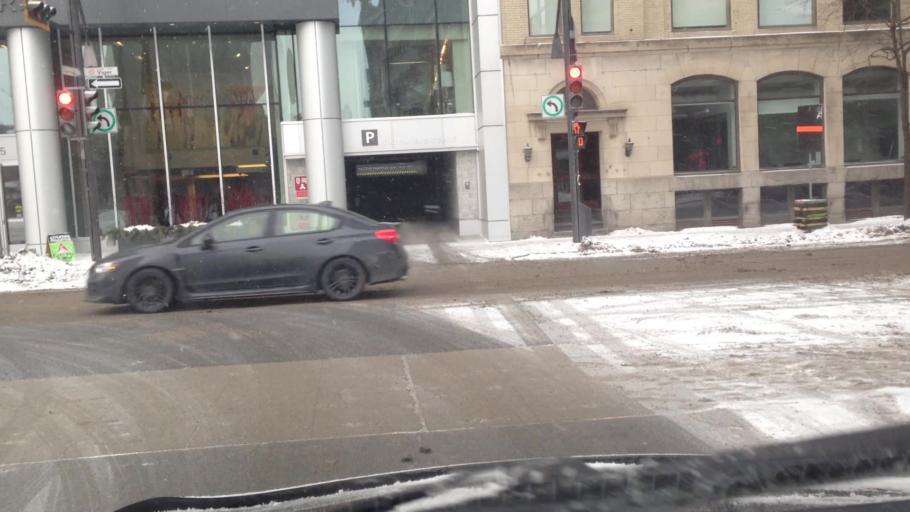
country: CA
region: Quebec
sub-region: Montreal
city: Montreal
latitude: 45.5022
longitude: -73.5628
